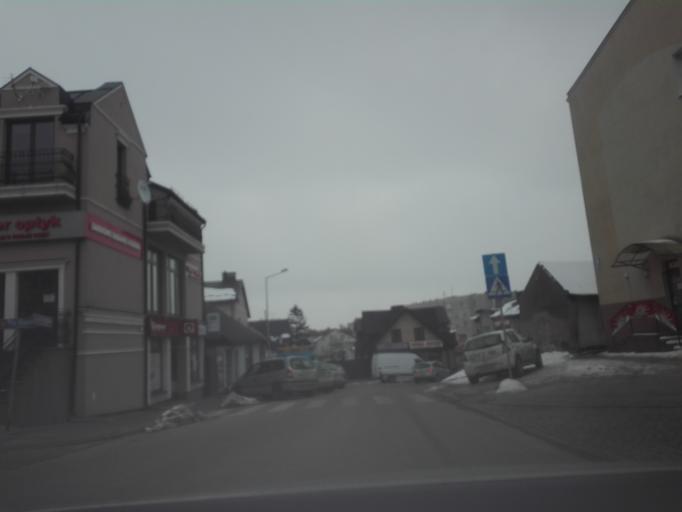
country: PL
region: Lublin Voivodeship
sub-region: Powiat hrubieszowski
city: Hrubieszow
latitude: 50.8059
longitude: 23.8923
